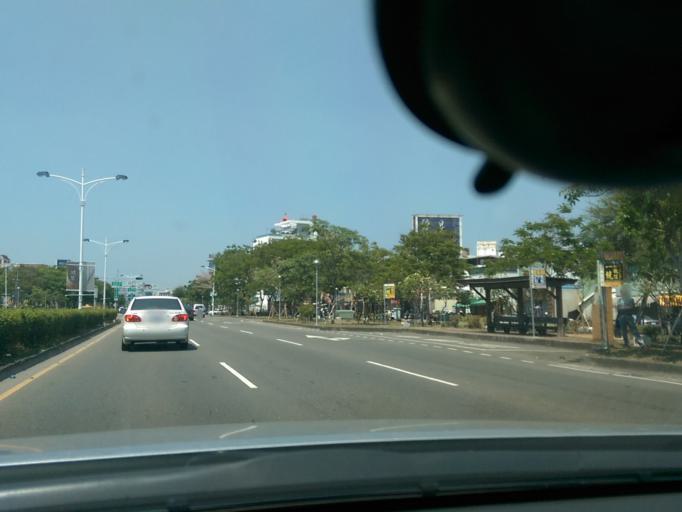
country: TW
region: Taiwan
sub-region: Chiayi
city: Jiayi Shi
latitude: 23.4911
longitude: 120.4528
